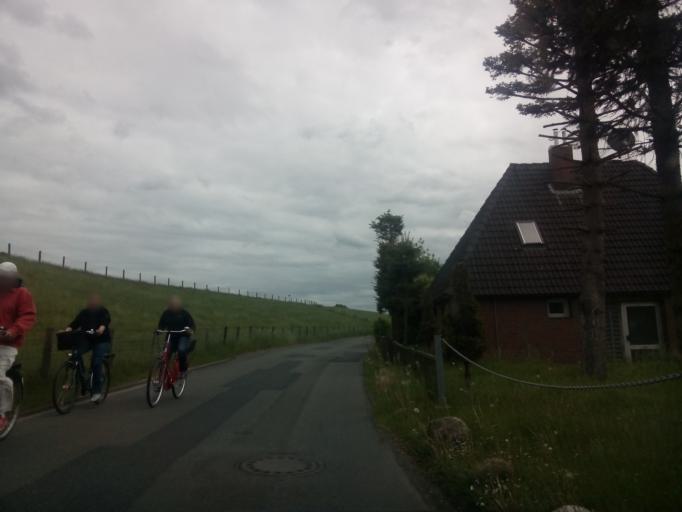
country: DE
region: Lower Saxony
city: Lemwerder
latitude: 53.1706
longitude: 8.5752
